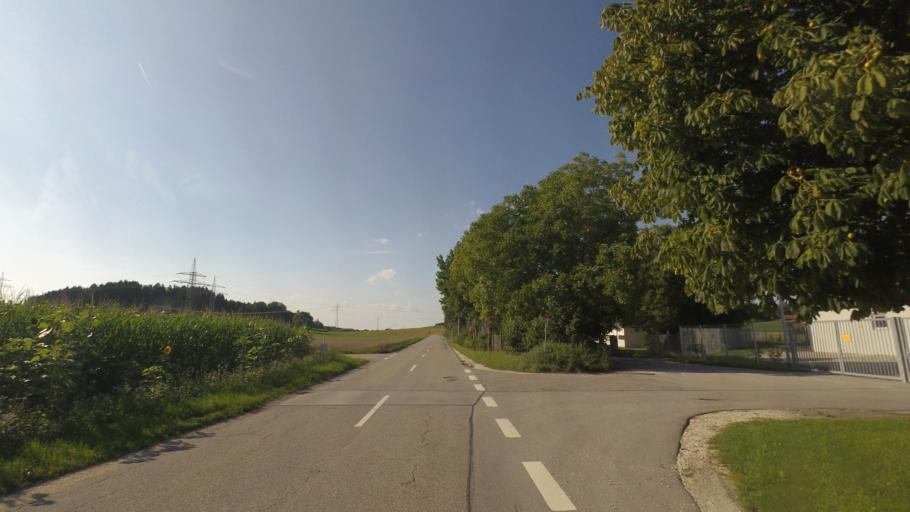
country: DE
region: Bavaria
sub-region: Upper Bavaria
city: Traunstein
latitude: 47.8814
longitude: 12.6193
